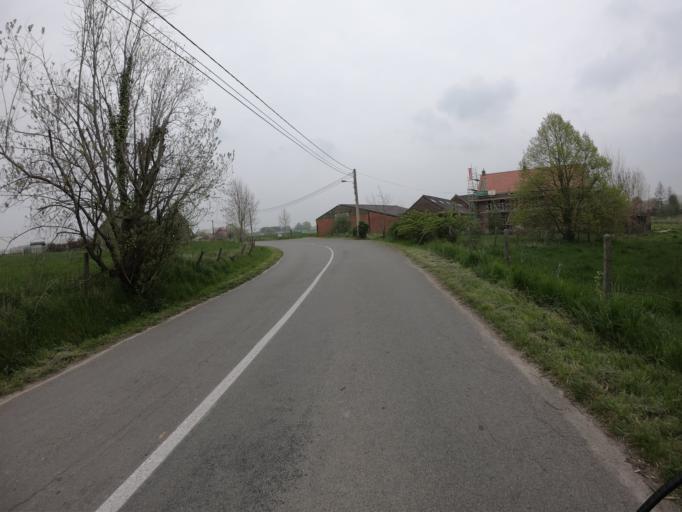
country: BE
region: Wallonia
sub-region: Province du Hainaut
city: Flobecq
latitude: 50.7385
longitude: 3.7519
